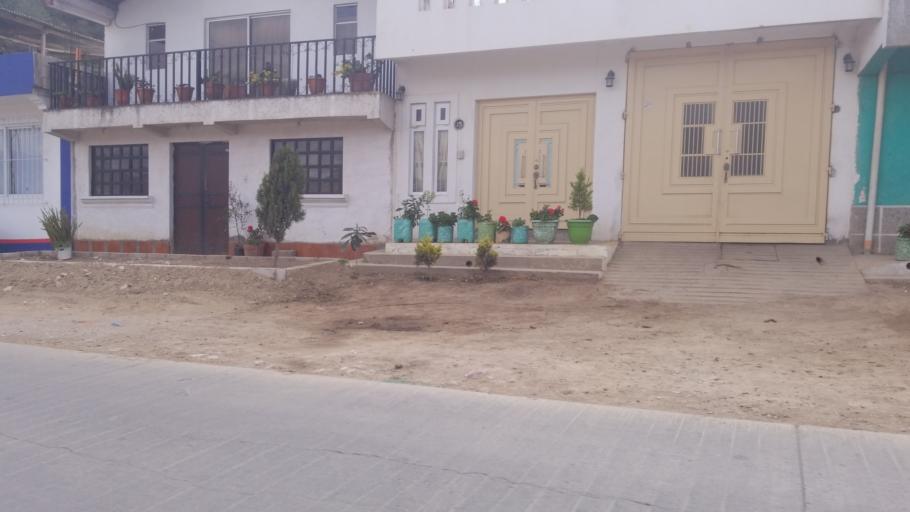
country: GT
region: Quetzaltenango
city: Quetzaltenango
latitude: 14.8188
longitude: -91.5370
